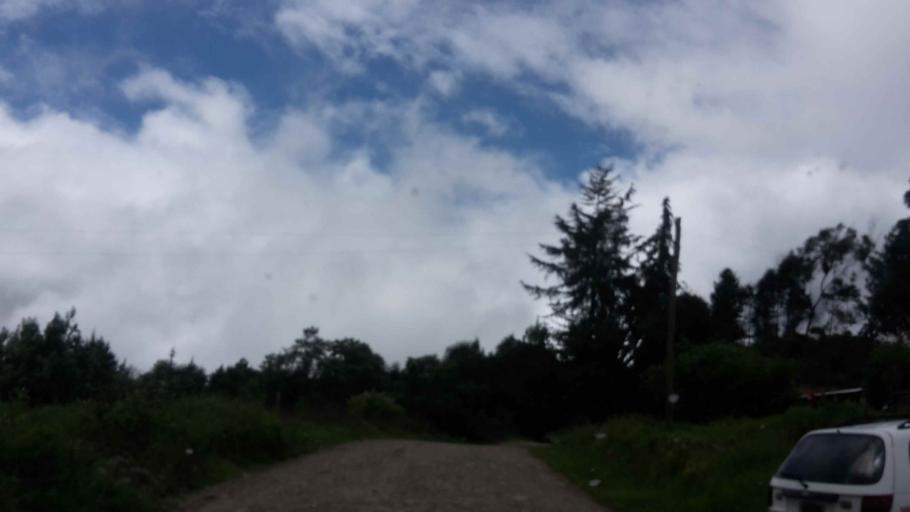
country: BO
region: Cochabamba
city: Colomi
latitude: -17.1285
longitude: -65.9366
